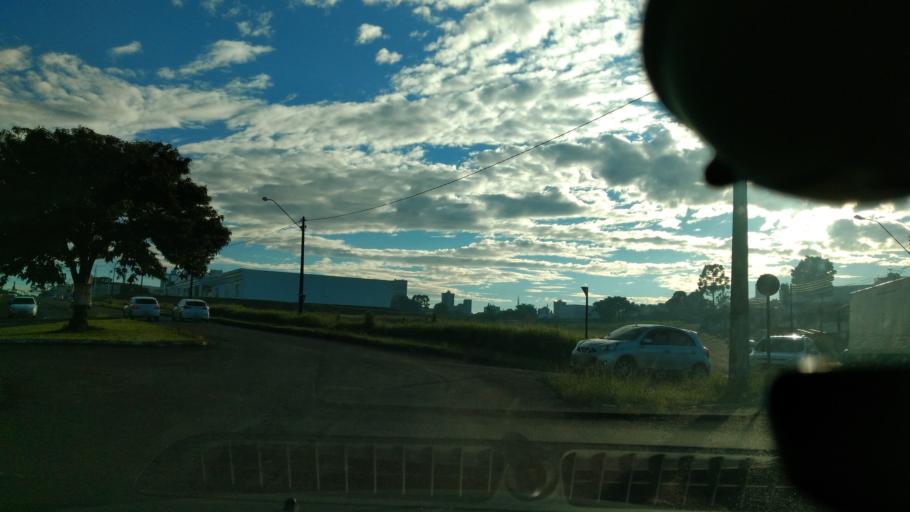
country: BR
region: Parana
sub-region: Guarapuava
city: Guarapuava
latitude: -25.3943
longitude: -51.4822
